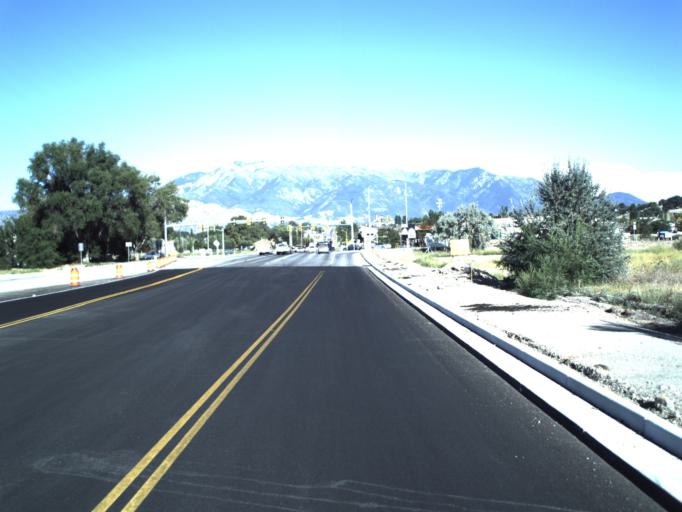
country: US
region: Utah
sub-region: Weber County
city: West Haven
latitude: 41.1905
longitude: -112.0508
